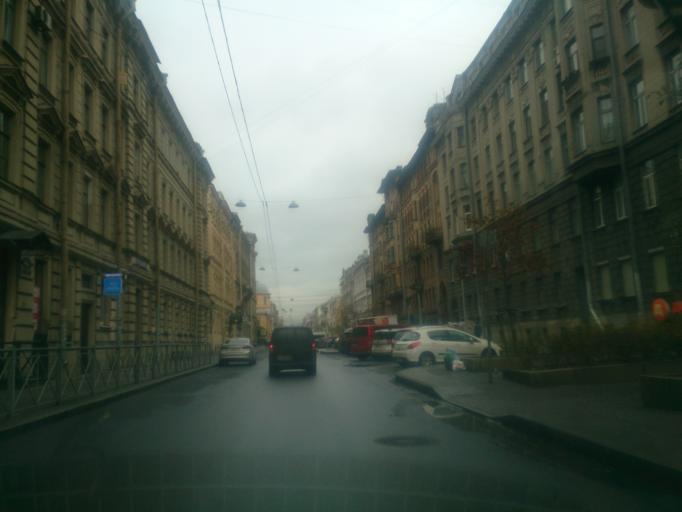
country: RU
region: St.-Petersburg
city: Centralniy
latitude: 59.9212
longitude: 30.3386
